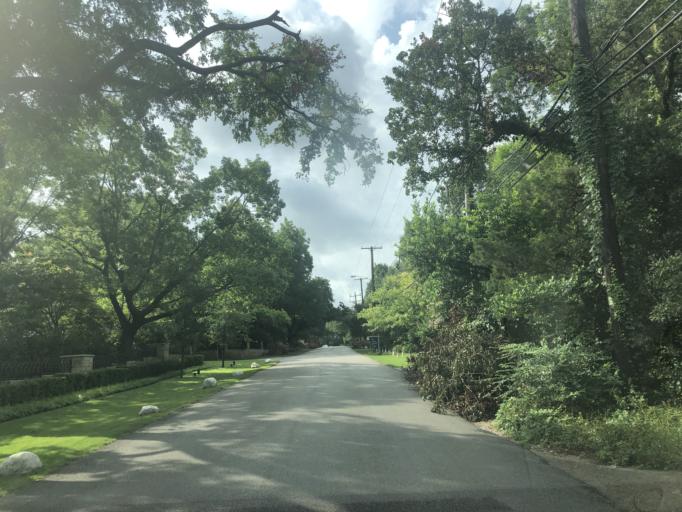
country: US
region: Texas
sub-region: Dallas County
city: University Park
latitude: 32.8621
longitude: -96.8276
